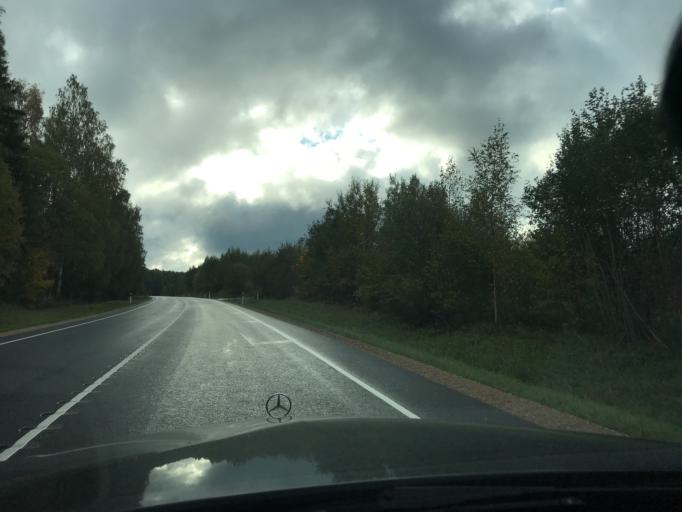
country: EE
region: Viljandimaa
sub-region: Karksi vald
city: Karksi-Nuia
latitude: 58.0560
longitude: 25.6321
